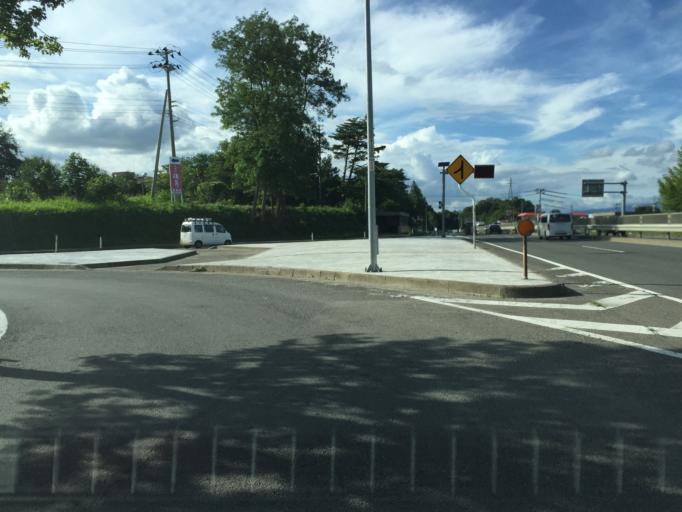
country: JP
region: Fukushima
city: Fukushima-shi
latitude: 37.6938
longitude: 140.4612
